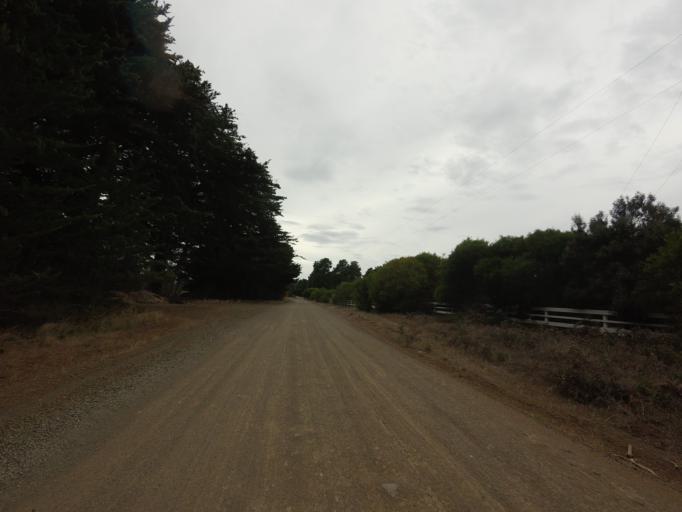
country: AU
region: Tasmania
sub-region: Clarence
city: Seven Mile Beach
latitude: -42.8365
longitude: 147.5288
